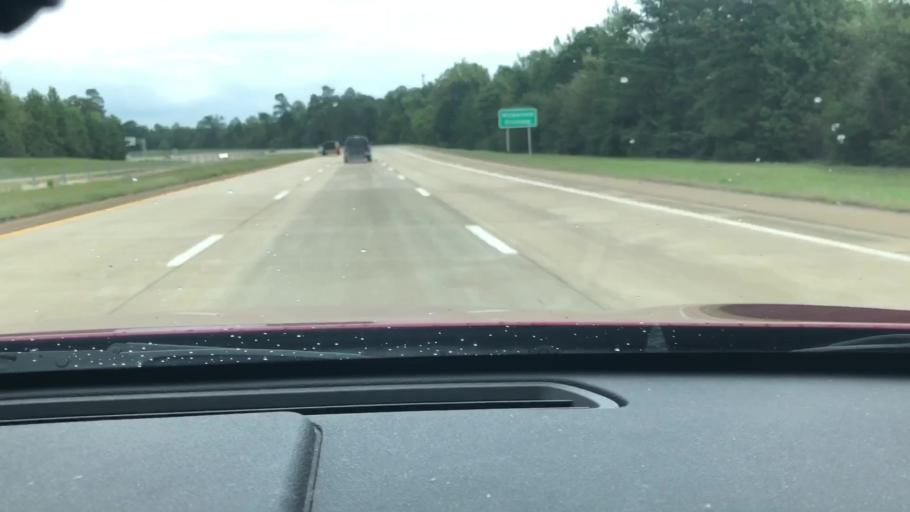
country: US
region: Texas
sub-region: Bowie County
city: Texarkana
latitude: 33.4020
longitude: -94.0066
